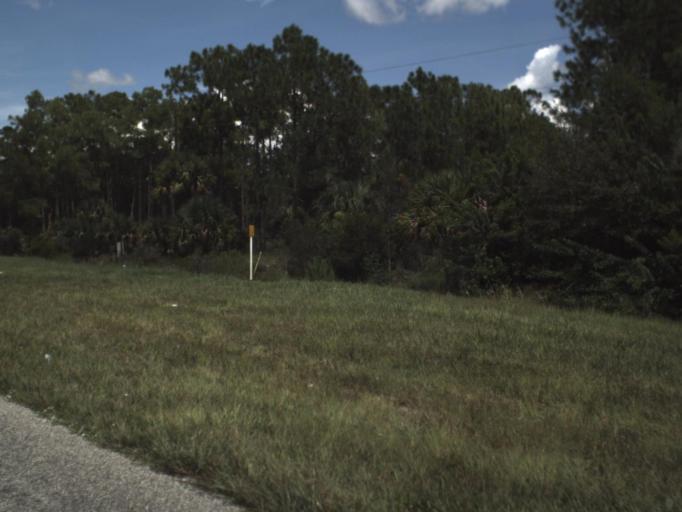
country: US
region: Florida
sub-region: Lee County
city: Burnt Store Marina
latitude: 26.8218
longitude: -81.9644
